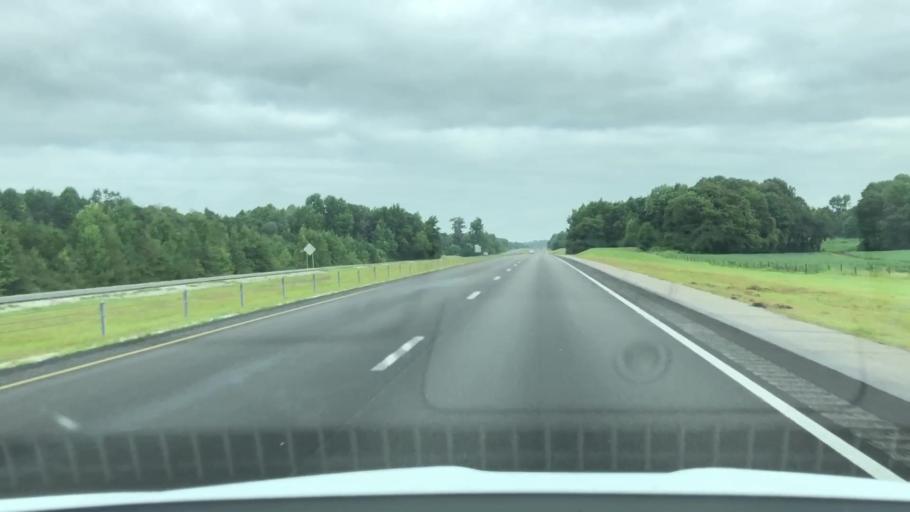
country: US
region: North Carolina
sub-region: Wayne County
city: Fremont
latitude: 35.5633
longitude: -77.9878
